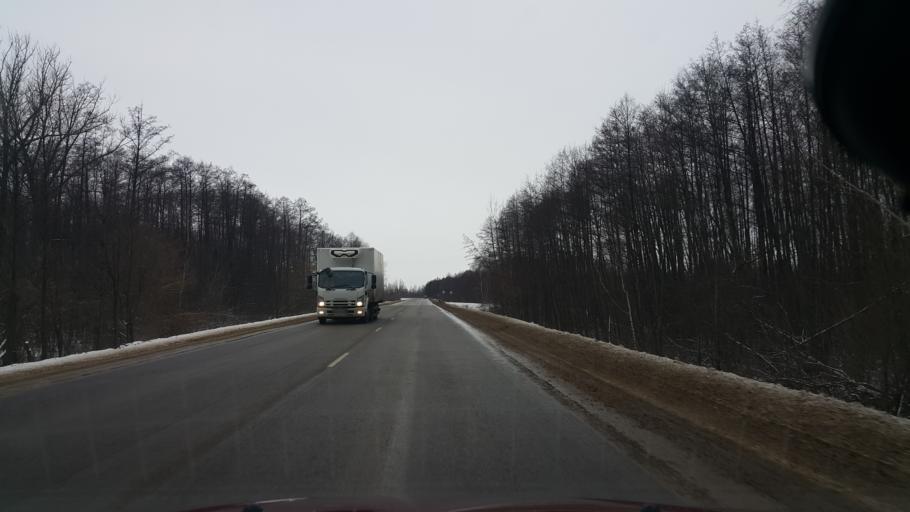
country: RU
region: Tambov
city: Kotovsk
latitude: 52.6299
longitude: 41.5081
